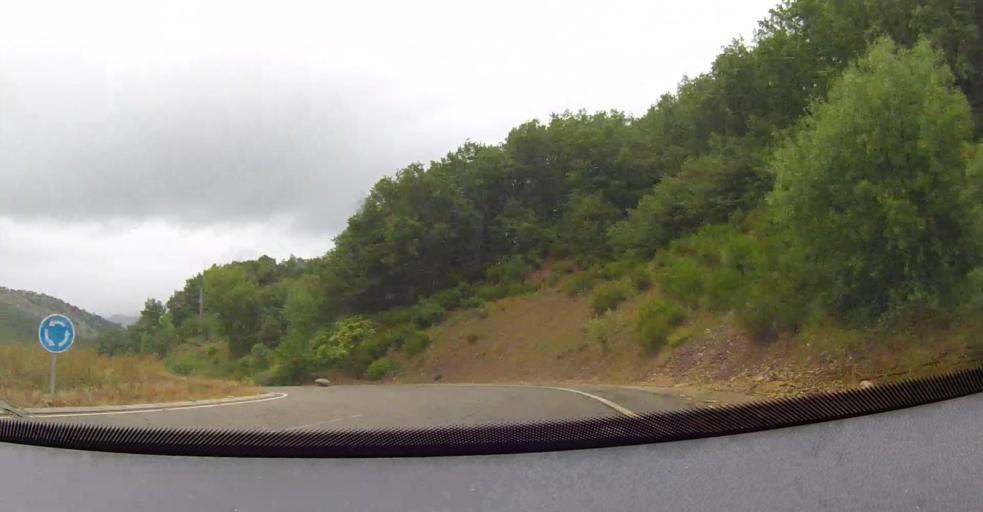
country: ES
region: Castille and Leon
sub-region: Provincia de Leon
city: Cistierna
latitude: 42.8130
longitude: -5.1310
